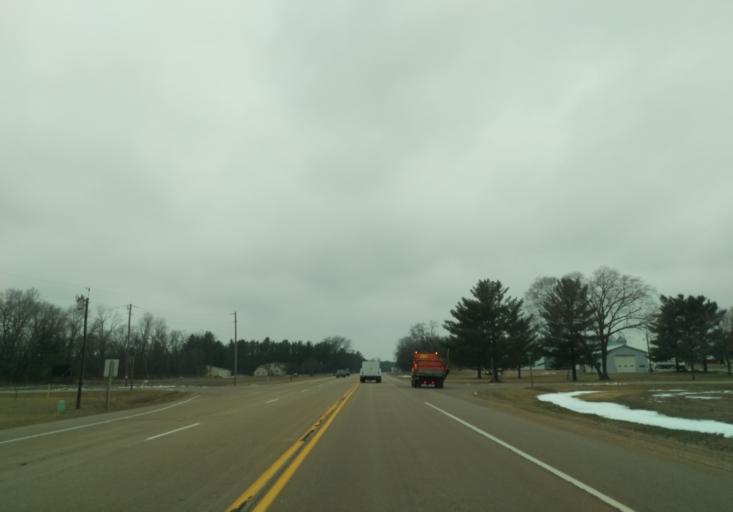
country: US
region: Wisconsin
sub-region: Sauk County
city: Spring Green
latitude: 43.1897
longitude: -90.1322
